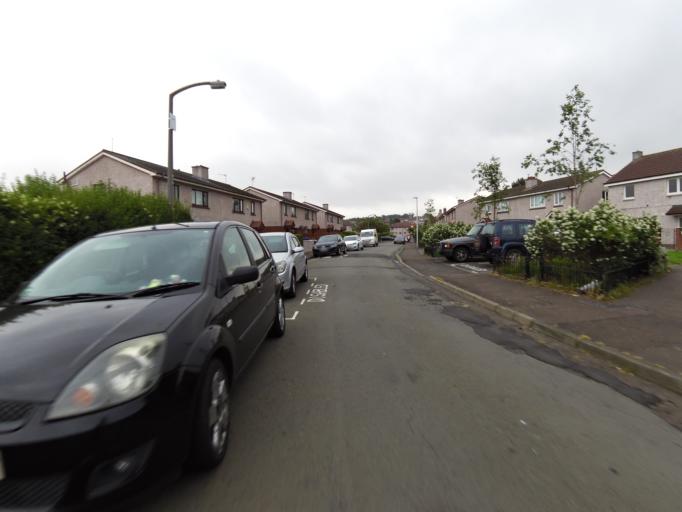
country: GB
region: Scotland
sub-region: Midlothian
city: Loanhead
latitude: 55.9144
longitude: -3.1344
